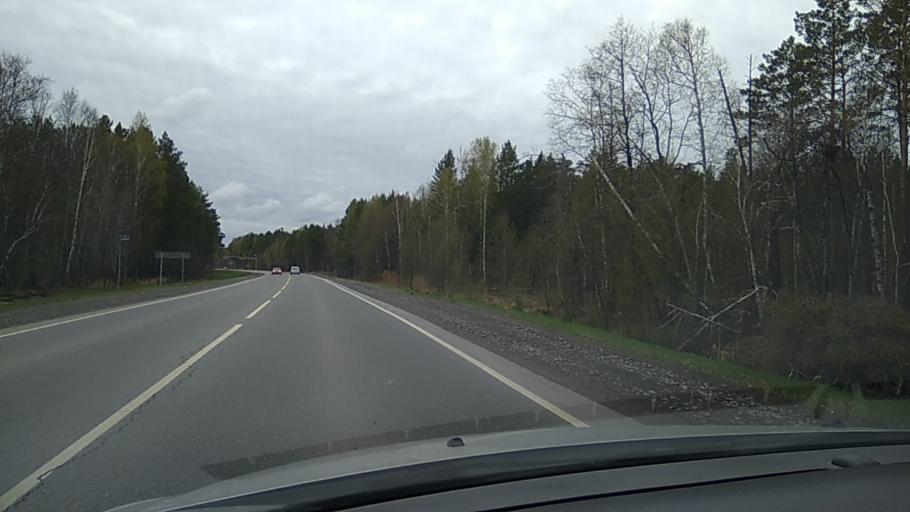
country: RU
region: Tjumen
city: Chervishevo
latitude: 56.9715
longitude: 65.4395
